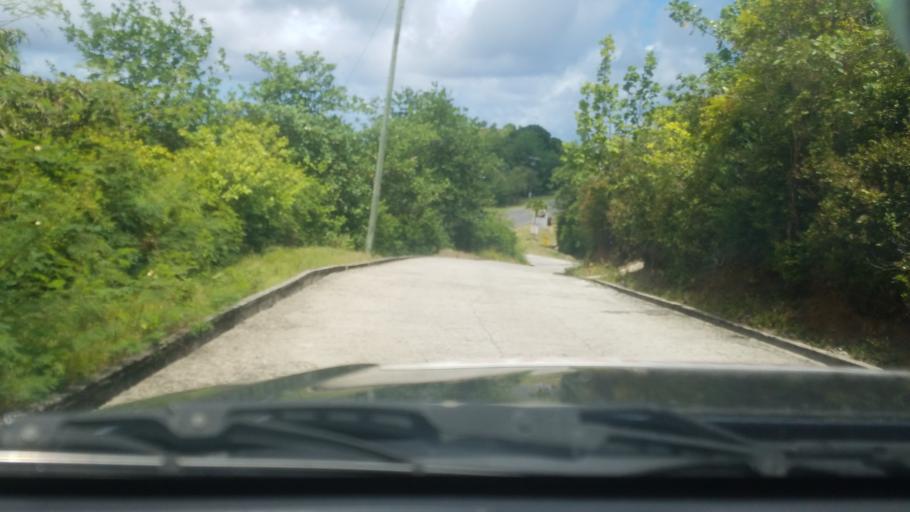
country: LC
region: Dennery Quarter
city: Dennery
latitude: 13.9202
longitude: -60.8972
